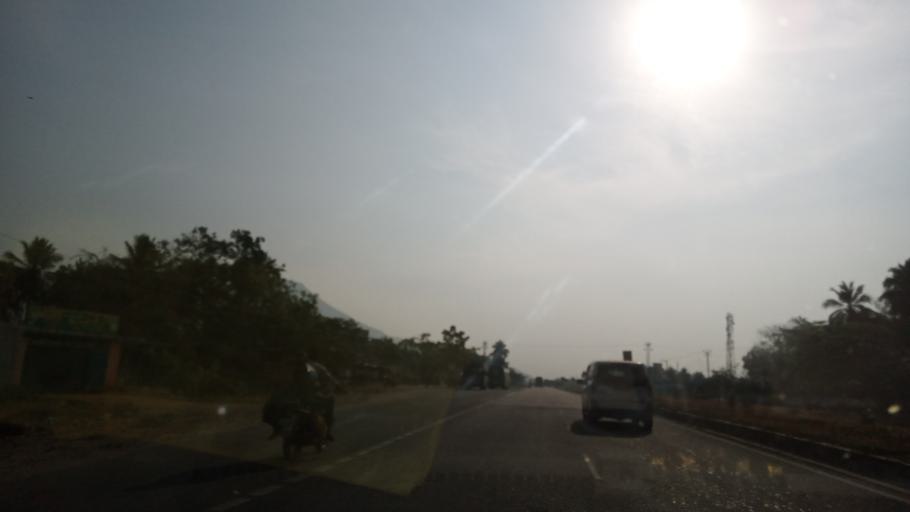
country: IN
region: Tamil Nadu
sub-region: Salem
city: Belur
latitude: 11.6651
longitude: 78.3110
